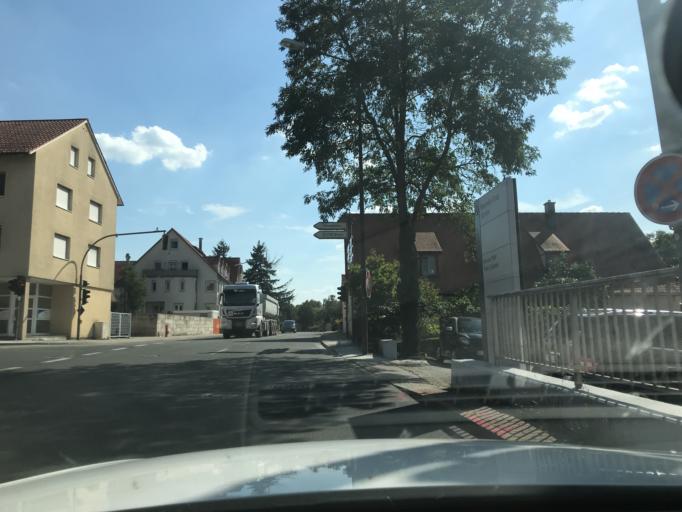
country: DE
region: Bavaria
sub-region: Regierungsbezirk Mittelfranken
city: Erlangen
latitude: 49.5712
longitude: 10.9850
